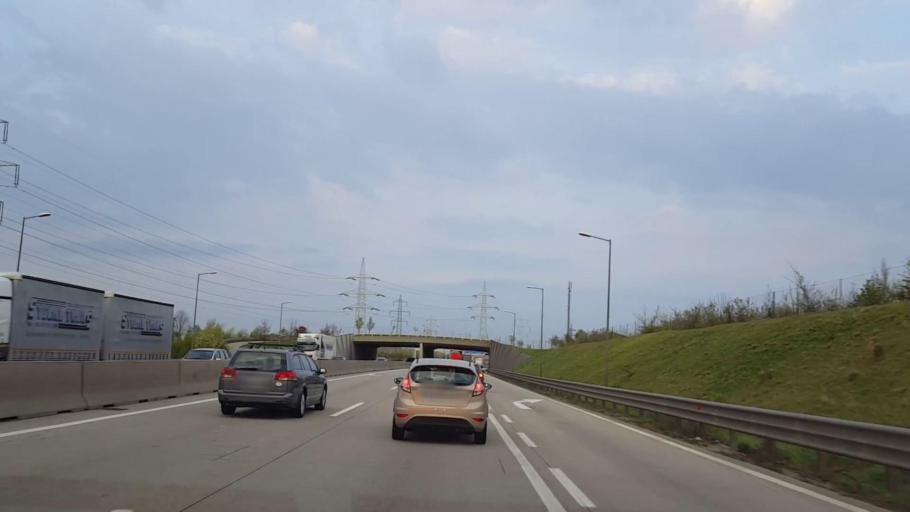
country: AT
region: Lower Austria
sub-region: Politischer Bezirk Wien-Umgebung
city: Leopoldsdorf
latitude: 48.1277
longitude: 16.3807
